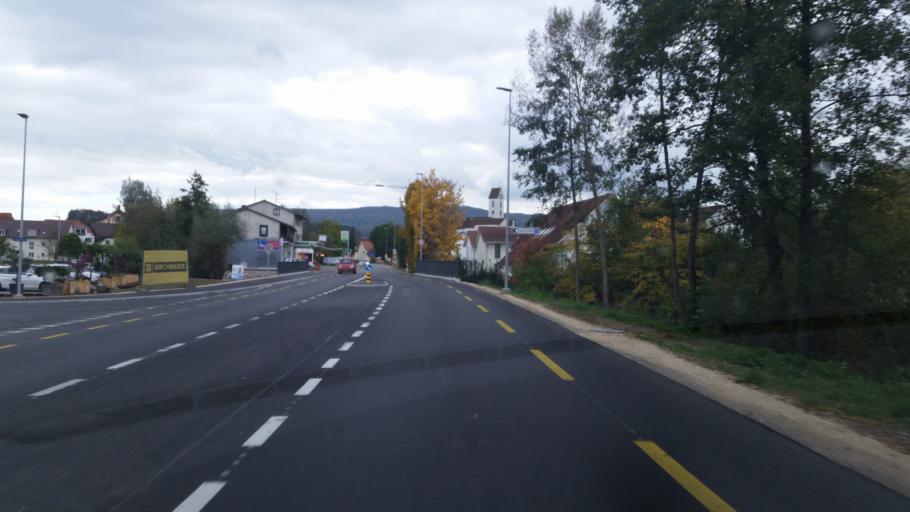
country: CH
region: Aargau
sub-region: Bezirk Baden
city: Unterehrendingen
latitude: 47.5229
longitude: 8.3267
